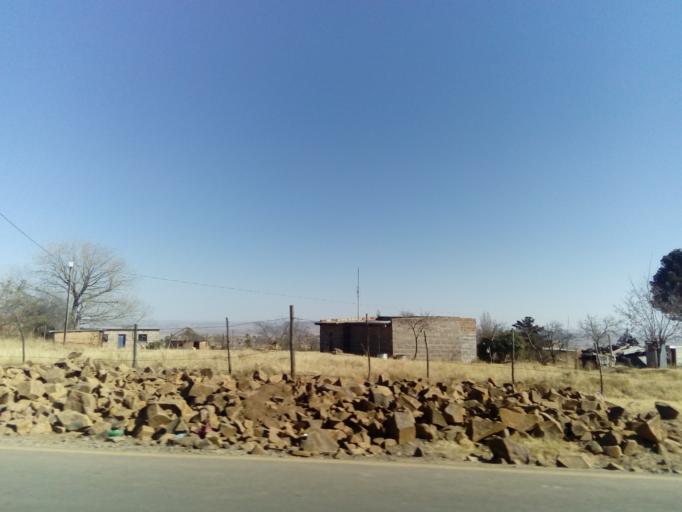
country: LS
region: Berea
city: Teyateyaneng
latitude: -29.1170
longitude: 27.8231
